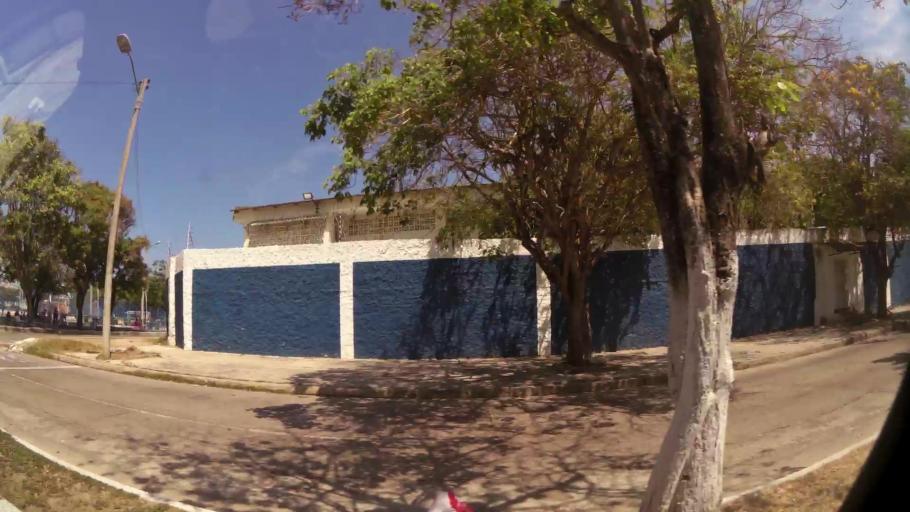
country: CO
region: Atlantico
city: Barranquilla
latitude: 10.9655
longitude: -74.7989
